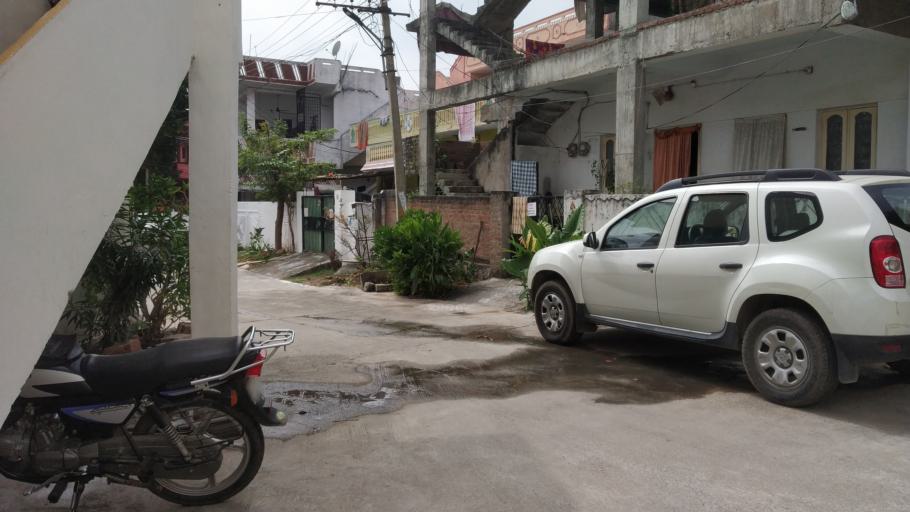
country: IN
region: Telangana
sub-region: Hyderabad
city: Malkajgiri
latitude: 17.4606
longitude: 78.5650
